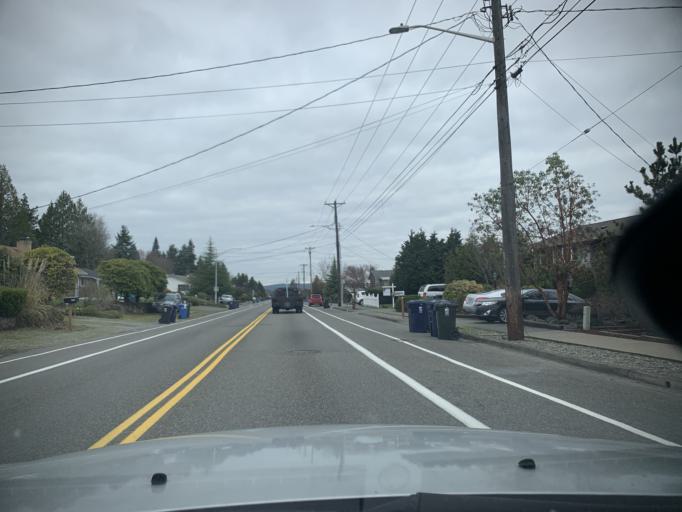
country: US
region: Washington
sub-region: Pierce County
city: Fircrest
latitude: 47.2862
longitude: -122.5211
